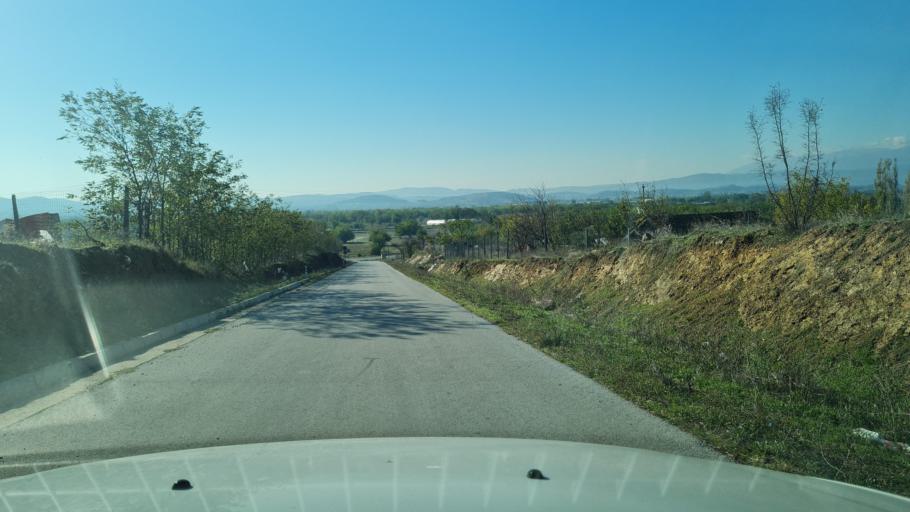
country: MK
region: Bogdanci
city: Bogdanci
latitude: 41.1943
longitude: 22.5632
